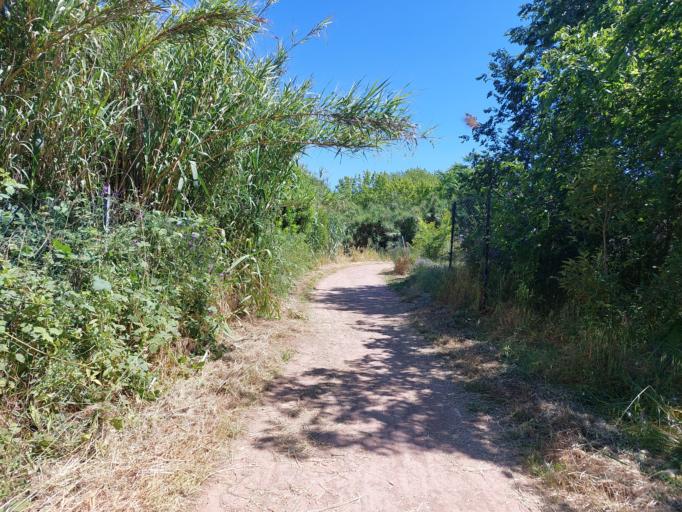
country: IT
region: Latium
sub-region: Citta metropolitana di Roma Capitale
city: Rome
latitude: 41.8561
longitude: 12.5486
